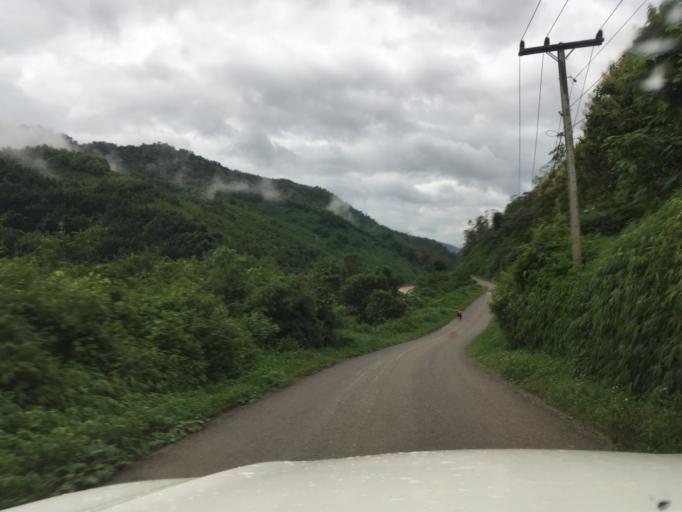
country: LA
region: Oudomxai
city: Muang La
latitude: 20.9983
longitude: 102.2319
